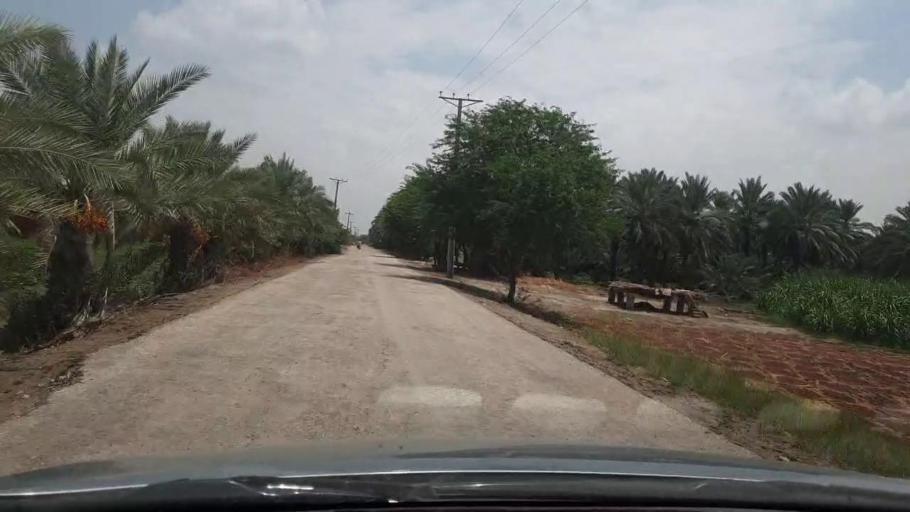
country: PK
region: Sindh
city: Khairpur
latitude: 27.4374
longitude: 68.7553
